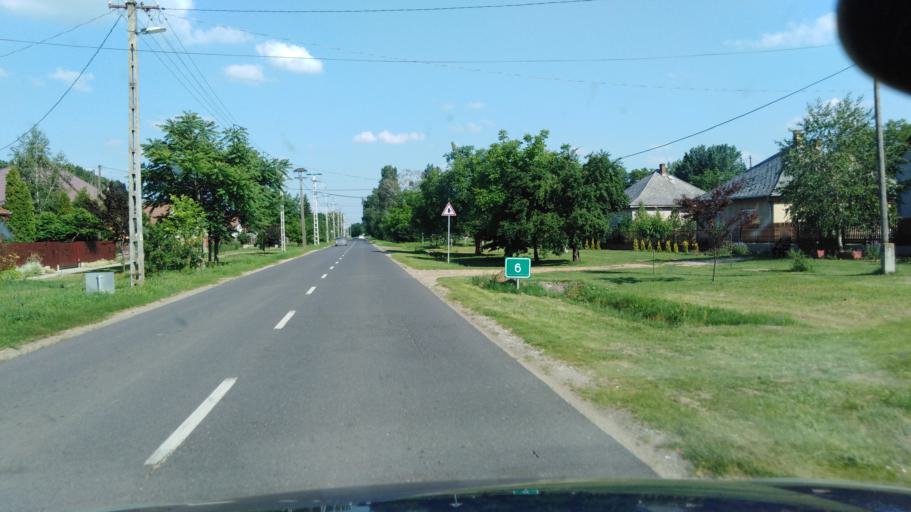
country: HU
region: Szabolcs-Szatmar-Bereg
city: Nyirvasvari
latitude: 47.8140
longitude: 22.1978
